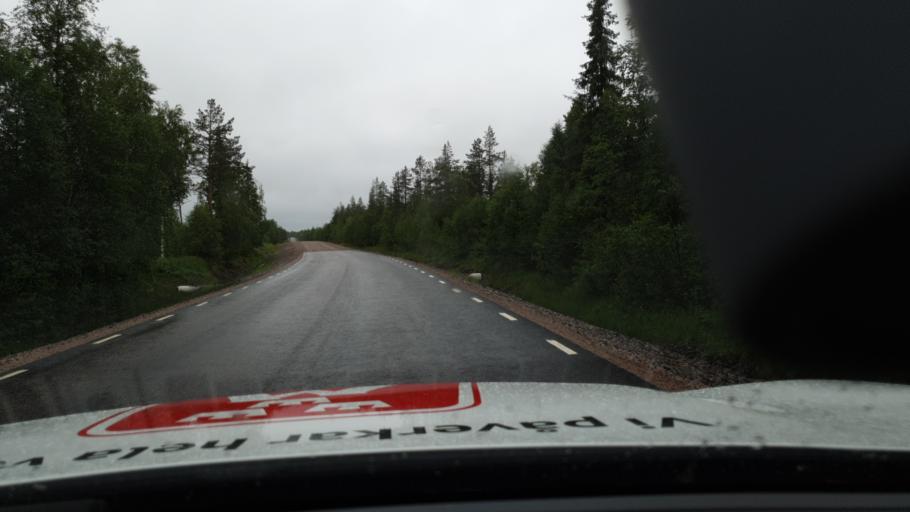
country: SE
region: Norrbotten
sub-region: Overtornea Kommun
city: OEvertornea
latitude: 66.5281
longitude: 23.3703
